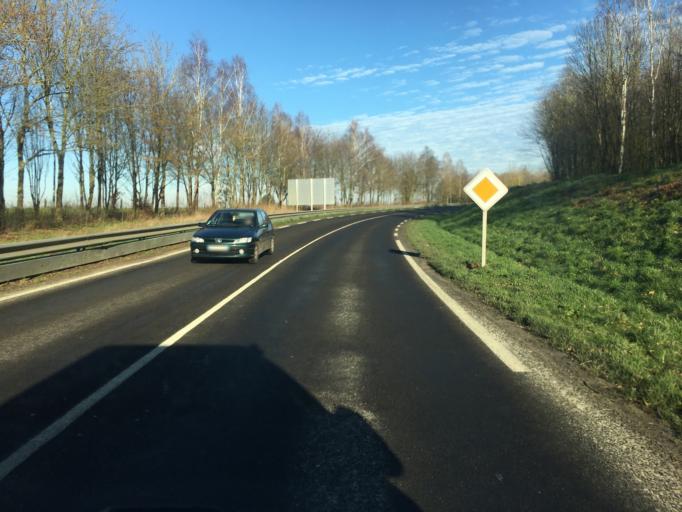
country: FR
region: Haute-Normandie
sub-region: Departement de la Seine-Maritime
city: Sainte-Marie-des-Champs
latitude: 49.6295
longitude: 0.8020
